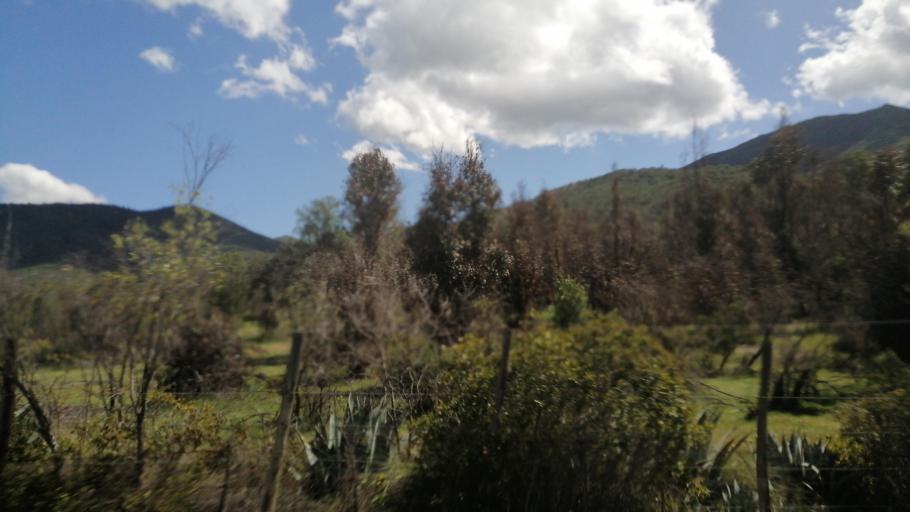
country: CL
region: Valparaiso
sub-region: Provincia de Marga Marga
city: Limache
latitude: -33.1831
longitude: -71.1870
